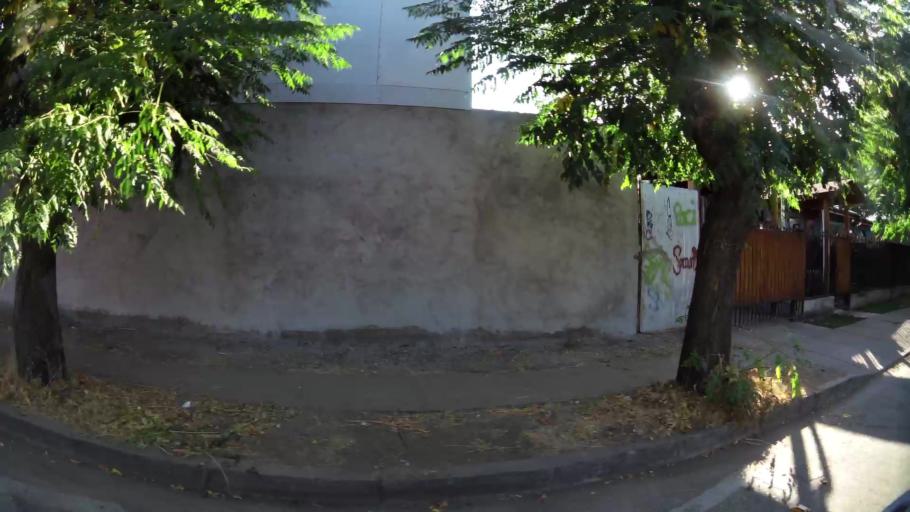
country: CL
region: Maule
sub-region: Provincia de Talca
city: Talca
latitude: -35.4376
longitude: -71.6871
